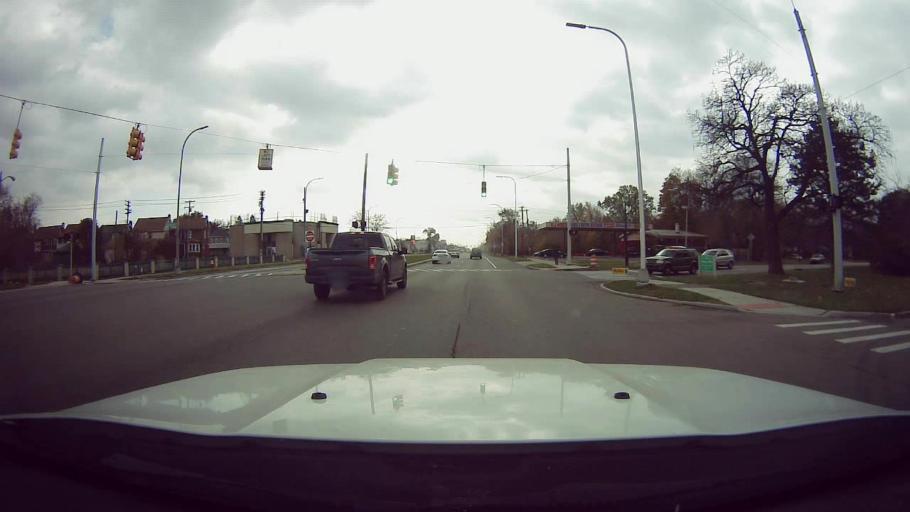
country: US
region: Michigan
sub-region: Wayne County
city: Highland Park
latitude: 42.3945
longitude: -83.1400
